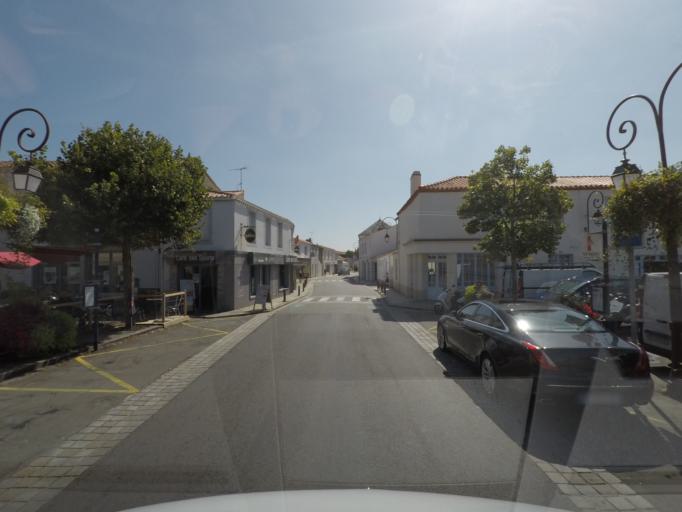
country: FR
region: Pays de la Loire
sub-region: Departement de la Vendee
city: Beauvoir-sur-Mer
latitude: 46.9156
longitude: -2.0429
